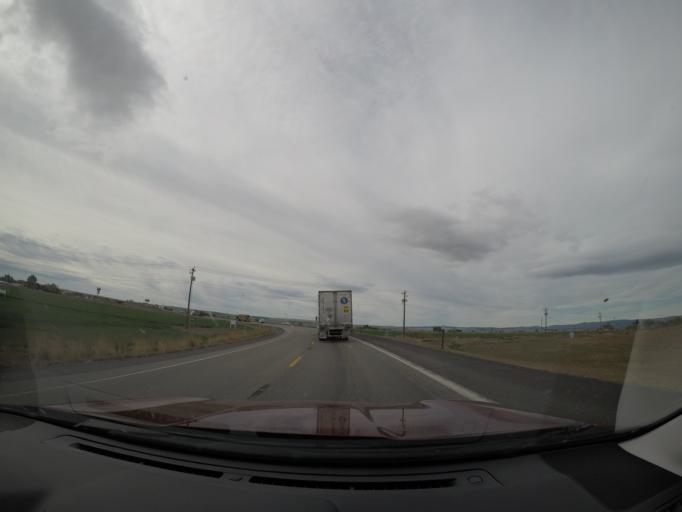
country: US
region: Washington
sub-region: Grant County
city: Quincy
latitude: 47.0891
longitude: -119.8632
